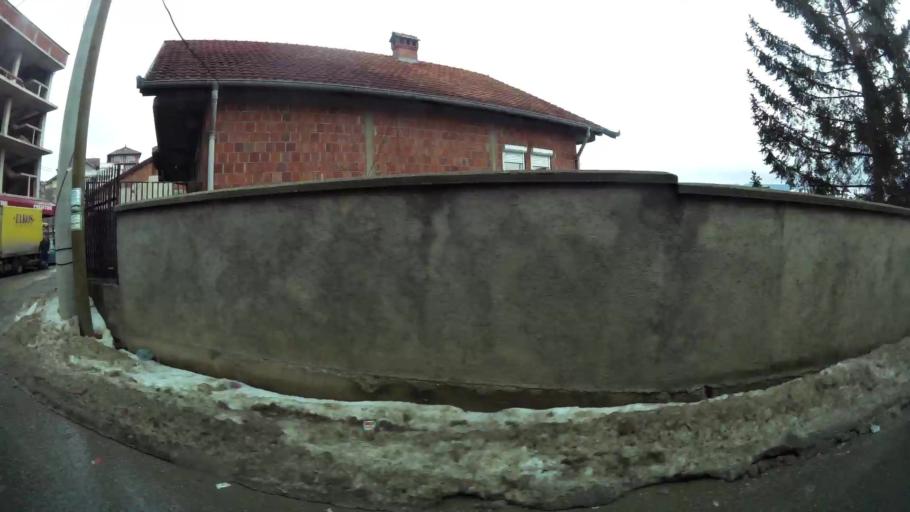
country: XK
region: Pristina
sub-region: Komuna e Prishtines
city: Pristina
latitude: 42.6813
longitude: 21.1704
